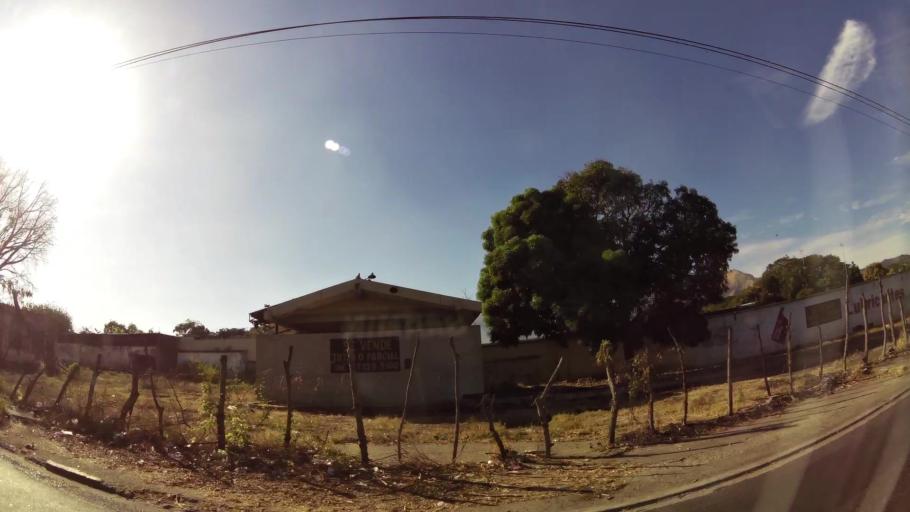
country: SV
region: Santa Ana
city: Santa Ana
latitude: 13.9998
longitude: -89.5515
